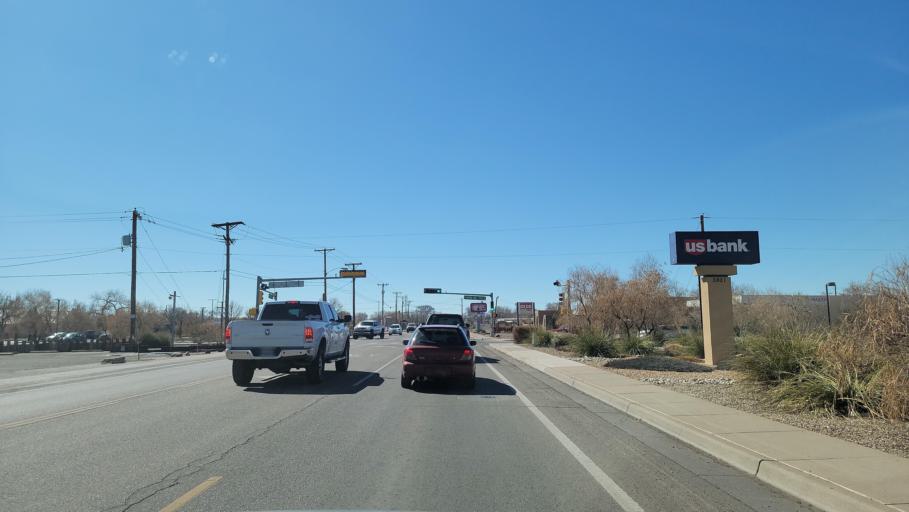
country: US
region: New Mexico
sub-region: Bernalillo County
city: South Valley
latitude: 35.0199
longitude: -106.6831
